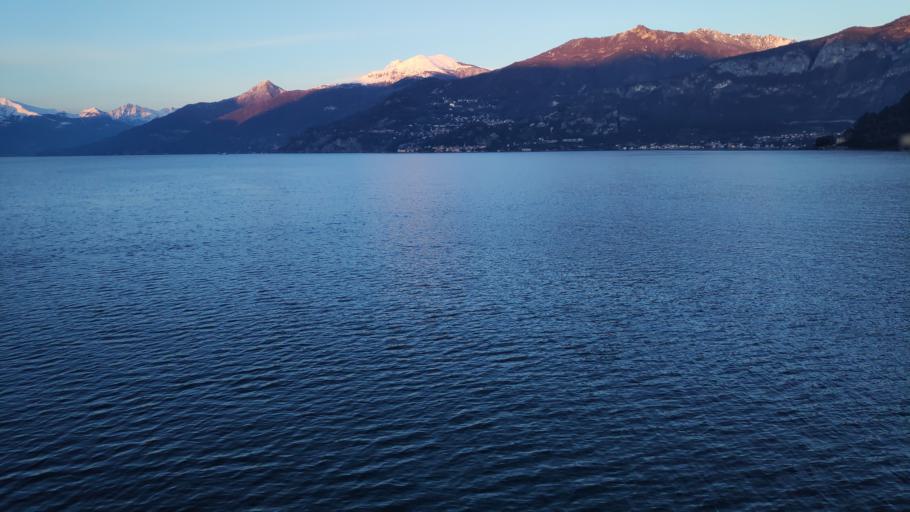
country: IT
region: Lombardy
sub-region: Provincia di Como
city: Cadenabbia
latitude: 45.9887
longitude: 9.2419
